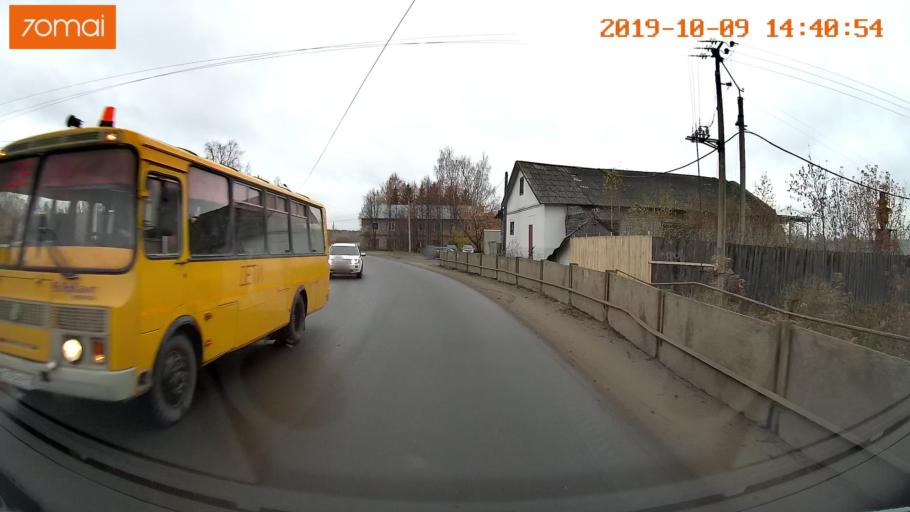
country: RU
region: Kostroma
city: Buy
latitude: 58.4742
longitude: 41.5277
